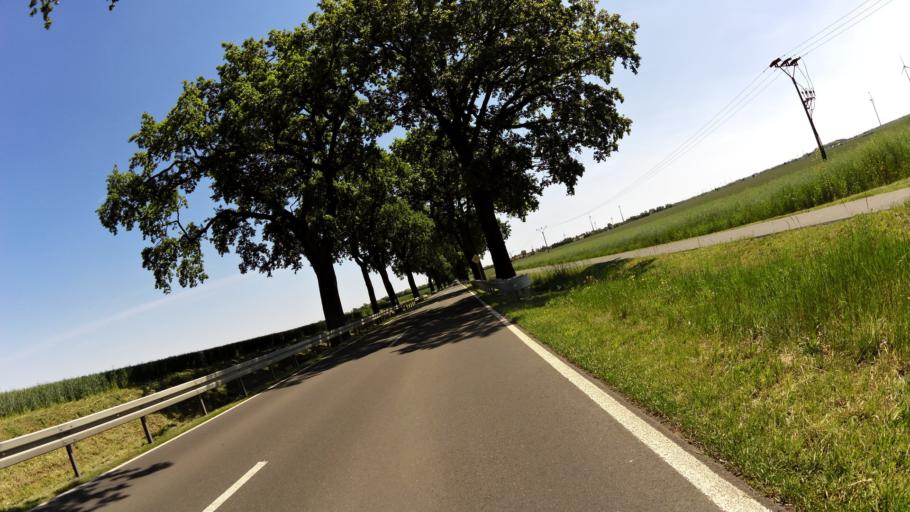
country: DE
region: Brandenburg
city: Seelow
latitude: 52.4870
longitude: 14.4237
